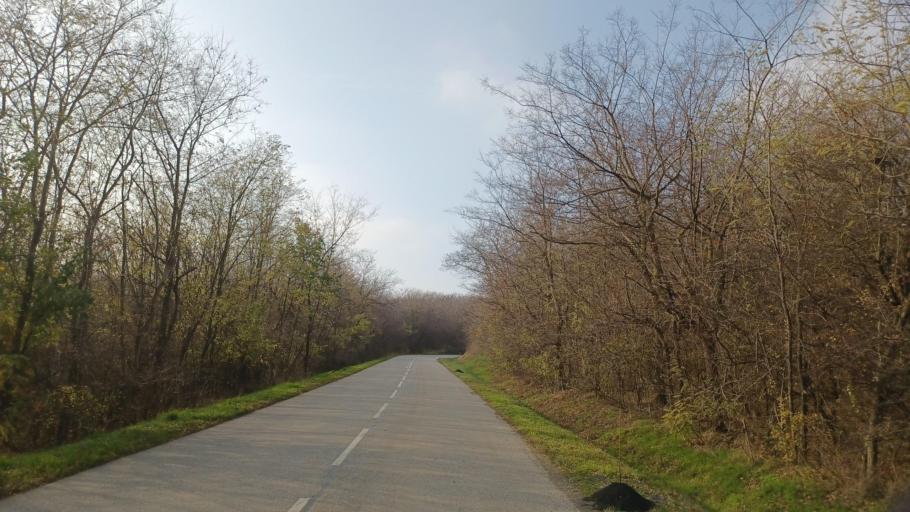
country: HU
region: Tolna
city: Tengelic
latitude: 46.5534
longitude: 18.7616
